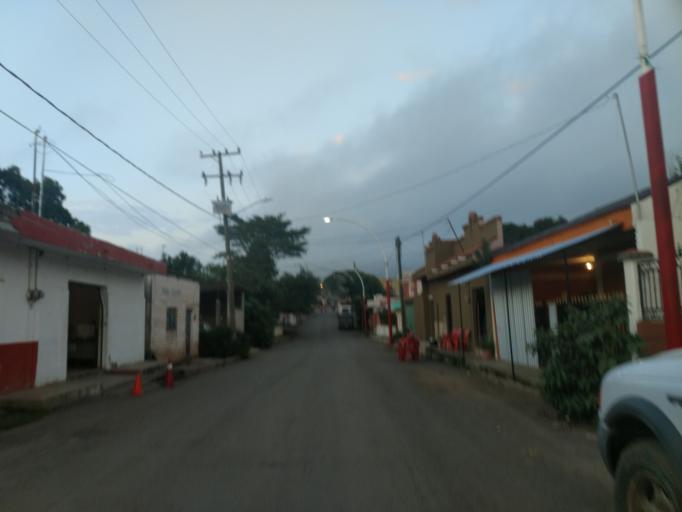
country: MX
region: Nayarit
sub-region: Tepic
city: La Corregidora
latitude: 21.4619
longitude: -104.8028
